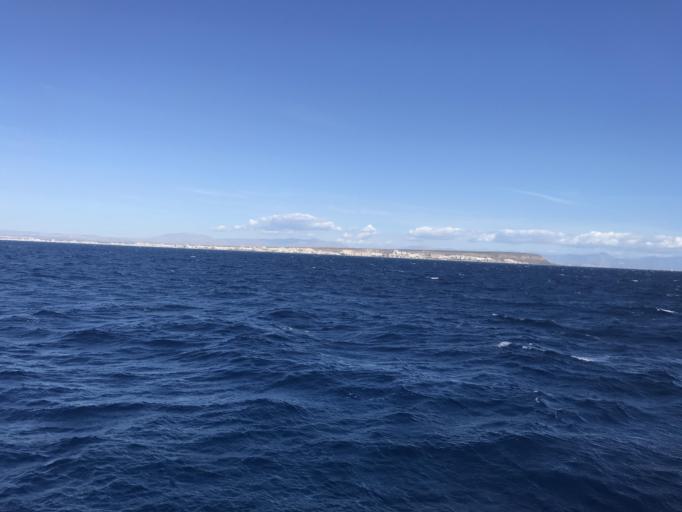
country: ES
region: Valencia
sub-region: Provincia de Alicante
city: Santa Pola
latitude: 38.1389
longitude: -0.5269
